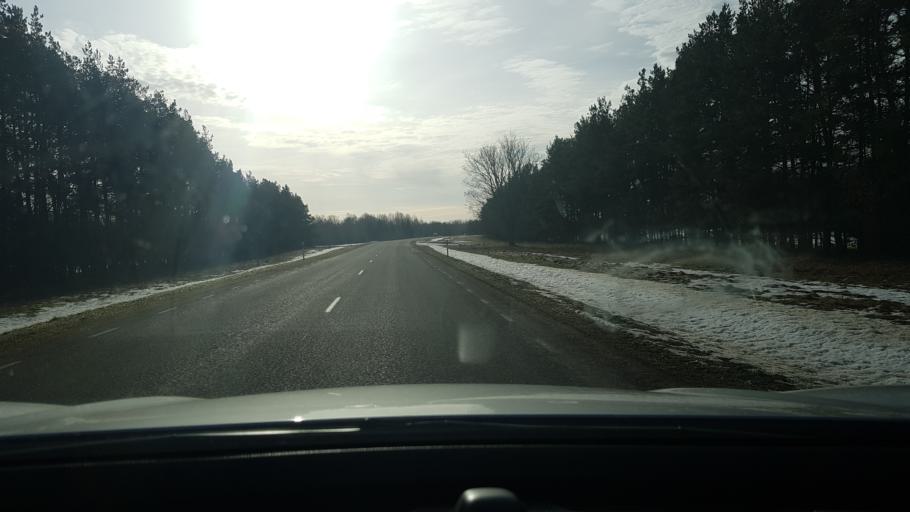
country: EE
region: Saare
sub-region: Kuressaare linn
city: Kuressaare
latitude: 58.5121
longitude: 22.7056
